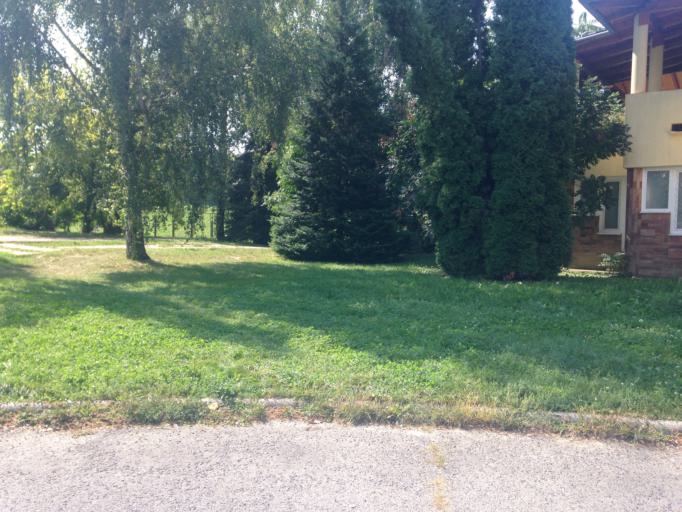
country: HU
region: Somogy
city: Kaposvar
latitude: 46.3703
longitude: 17.7959
